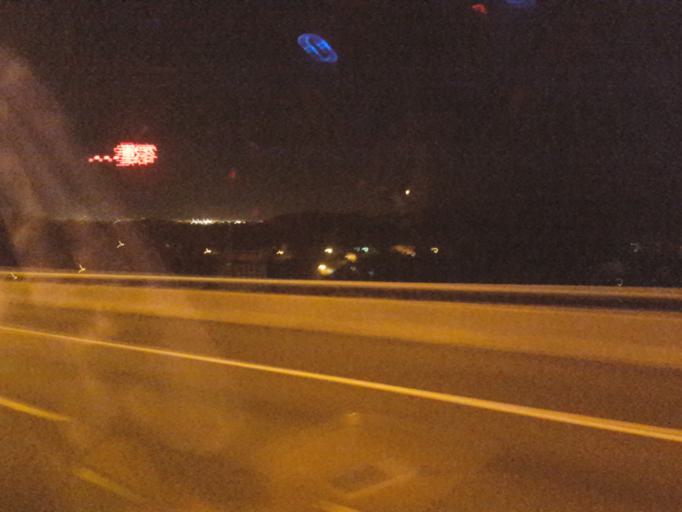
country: TW
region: Taiwan
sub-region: Taoyuan
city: Taoyuan
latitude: 25.0649
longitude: 121.3405
